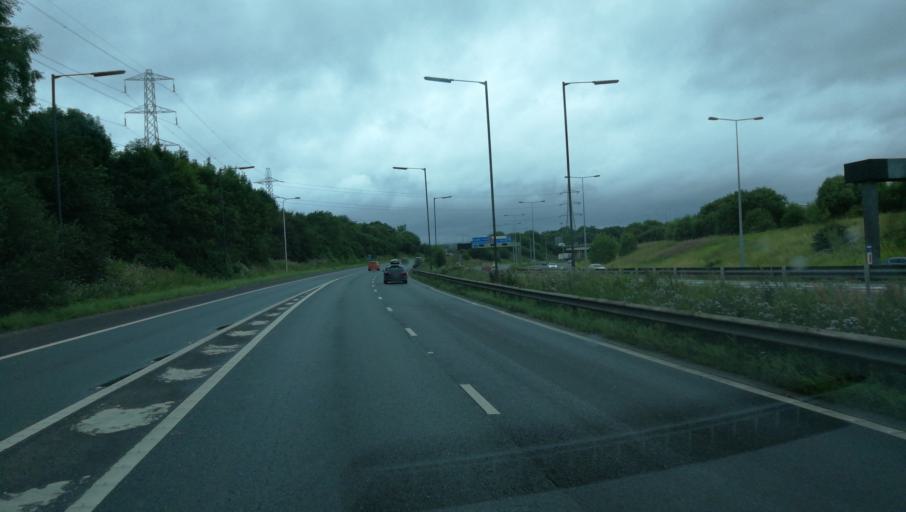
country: GB
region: England
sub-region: Borough of Bolton
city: Kearsley
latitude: 53.5332
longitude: -2.3887
